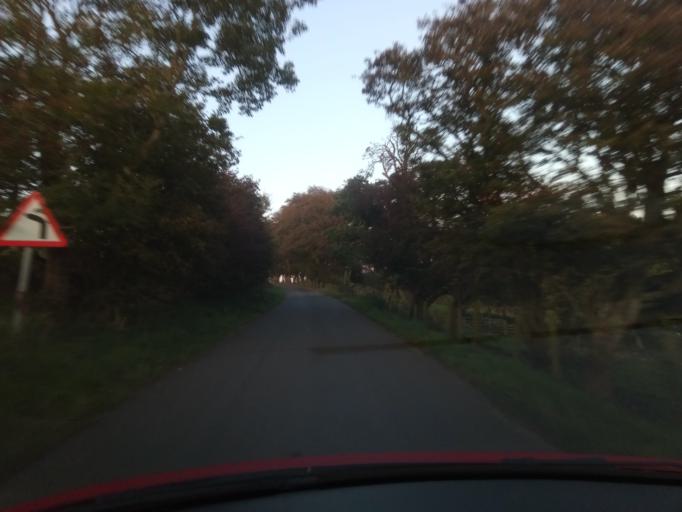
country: GB
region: Scotland
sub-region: Fife
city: Pathhead
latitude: 55.7918
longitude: -2.8913
